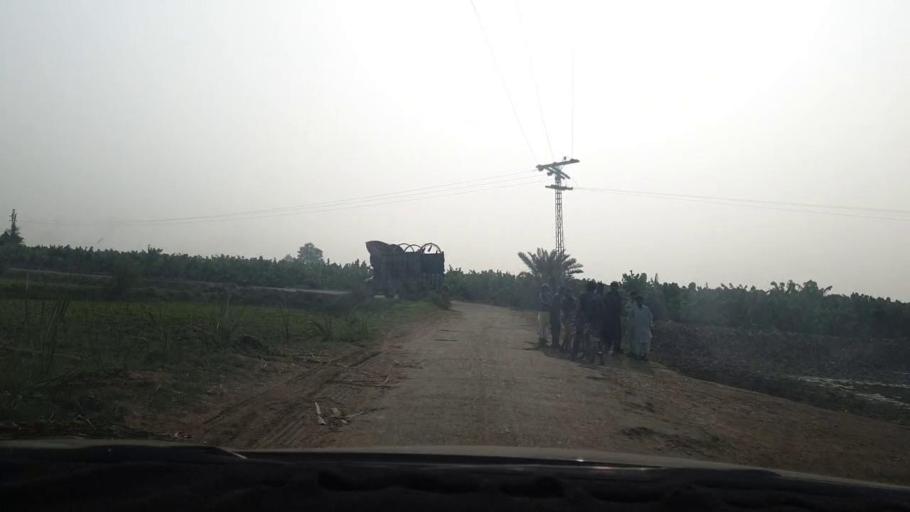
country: PK
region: Sindh
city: Matiari
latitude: 25.5935
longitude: 68.5378
